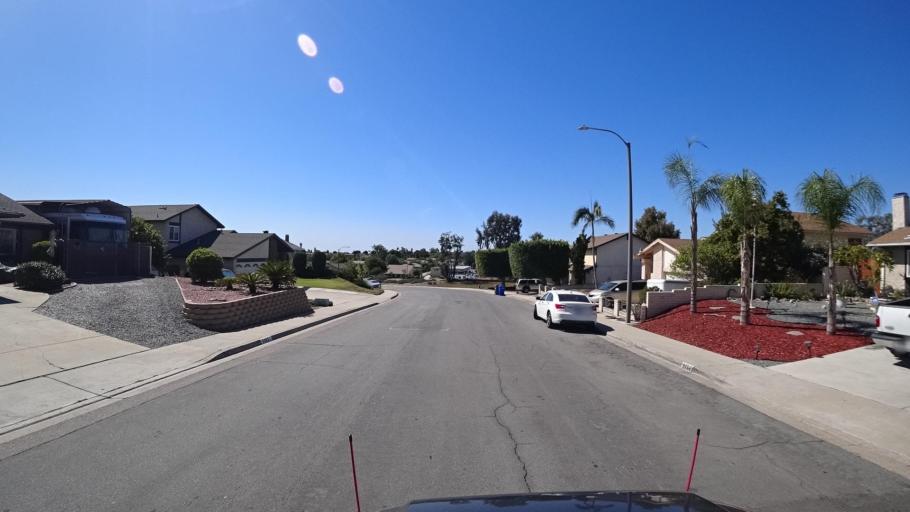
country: US
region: California
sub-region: San Diego County
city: La Presa
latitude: 32.6975
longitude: -117.0167
